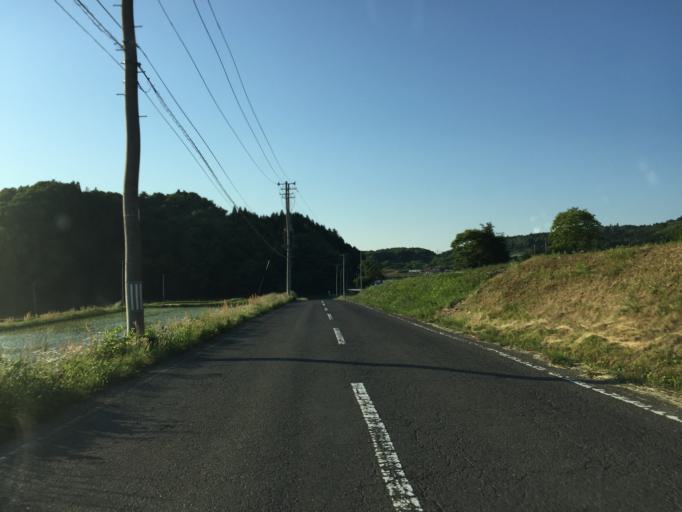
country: JP
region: Fukushima
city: Ishikawa
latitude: 37.0097
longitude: 140.4341
